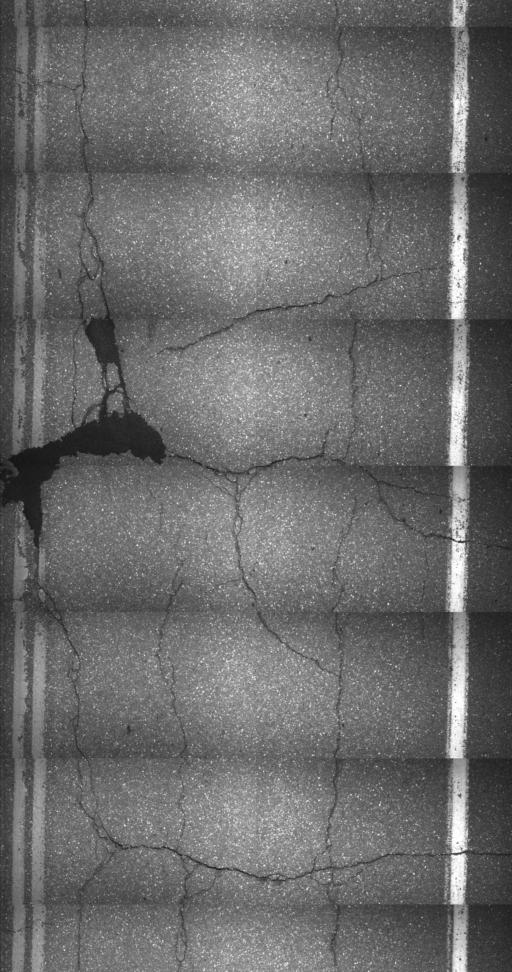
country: US
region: Vermont
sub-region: Orleans County
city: Newport
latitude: 44.8333
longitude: -72.4324
